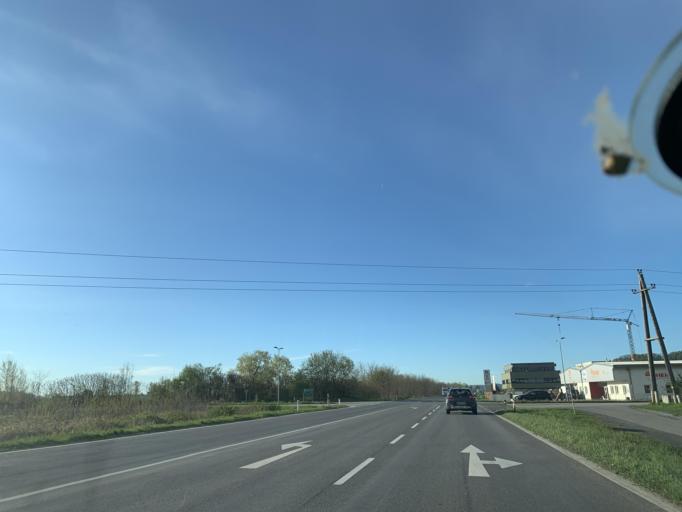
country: AT
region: Styria
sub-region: Politischer Bezirk Leibnitz
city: Lang
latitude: 46.8201
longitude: 15.5243
